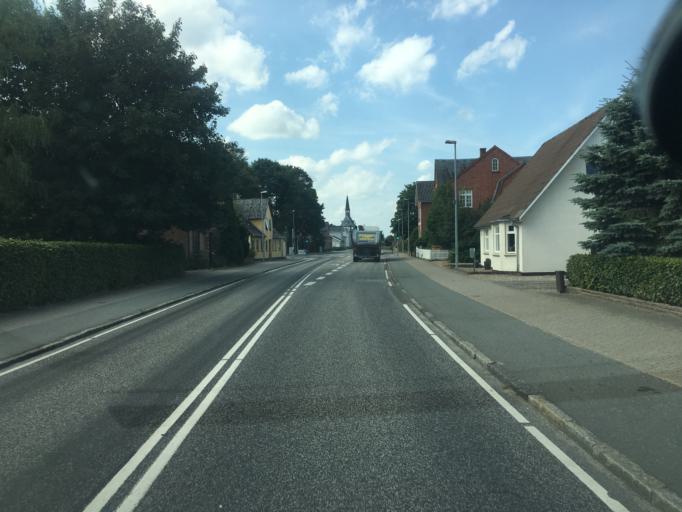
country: DK
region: South Denmark
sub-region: Aabenraa Kommune
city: Tinglev
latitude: 54.9352
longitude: 9.2482
